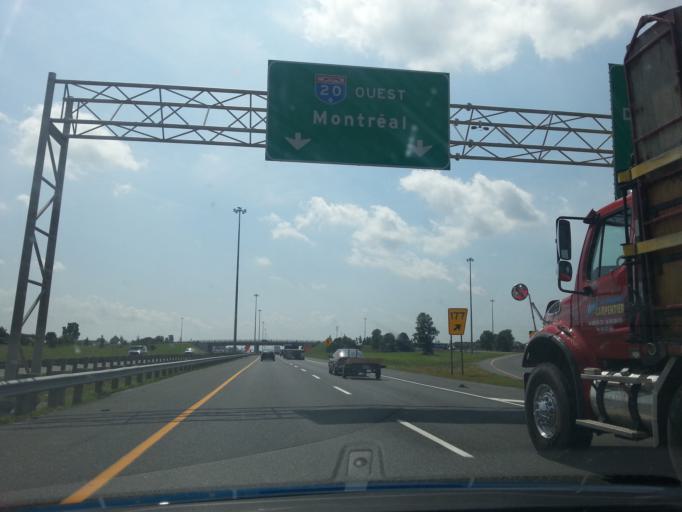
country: CA
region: Quebec
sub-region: Centre-du-Quebec
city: Drummondville
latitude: 45.9038
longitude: -72.5234
